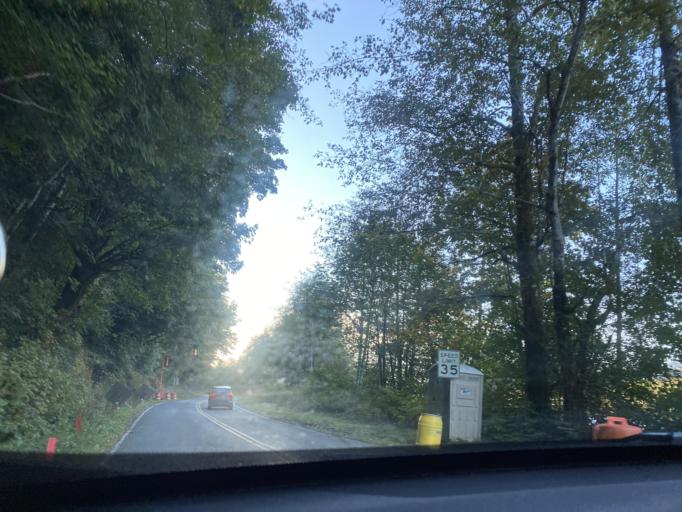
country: US
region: Washington
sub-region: Clallam County
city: Forks
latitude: 47.8207
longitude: -124.1801
